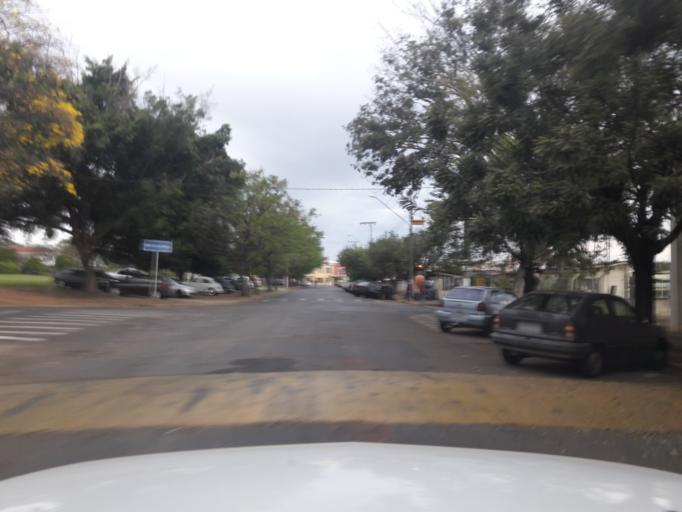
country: BR
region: Sao Paulo
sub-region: Moji-Guacu
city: Mogi-Gaucu
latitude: -22.3654
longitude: -46.9489
